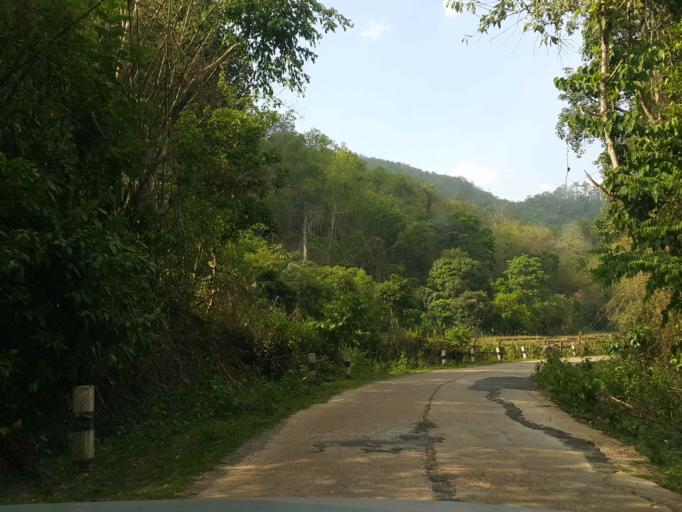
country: TH
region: Chiang Mai
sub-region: Amphoe Chiang Dao
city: Chiang Dao
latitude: 19.4069
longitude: 98.7866
